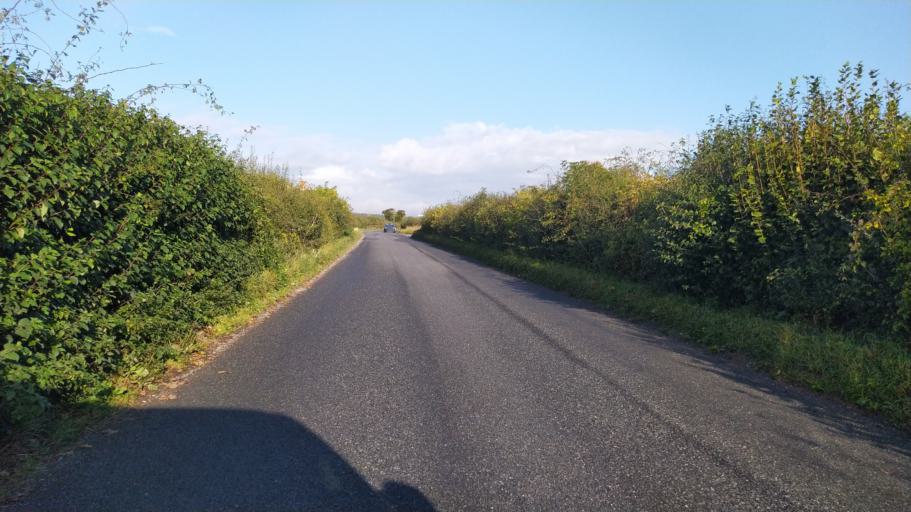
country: GB
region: England
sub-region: Wiltshire
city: Ansty
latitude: 50.9313
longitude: -2.0629
